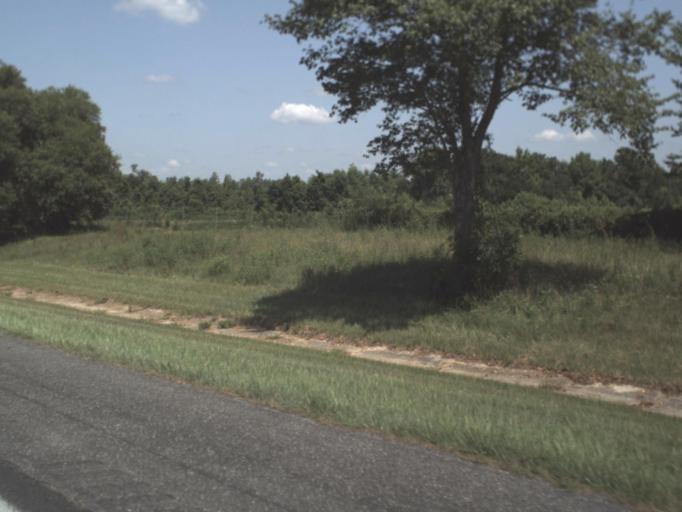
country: US
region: Florida
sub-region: Madison County
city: Madison
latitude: 30.4325
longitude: -83.5453
